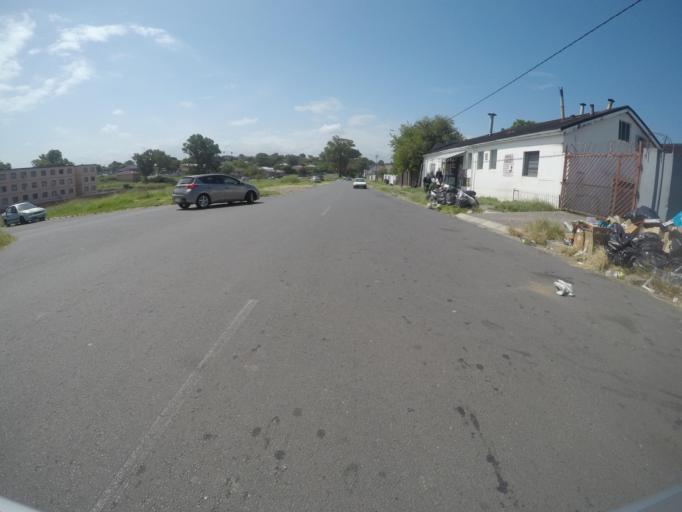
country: ZA
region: Eastern Cape
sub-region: Buffalo City Metropolitan Municipality
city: East London
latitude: -32.9807
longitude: 27.8827
